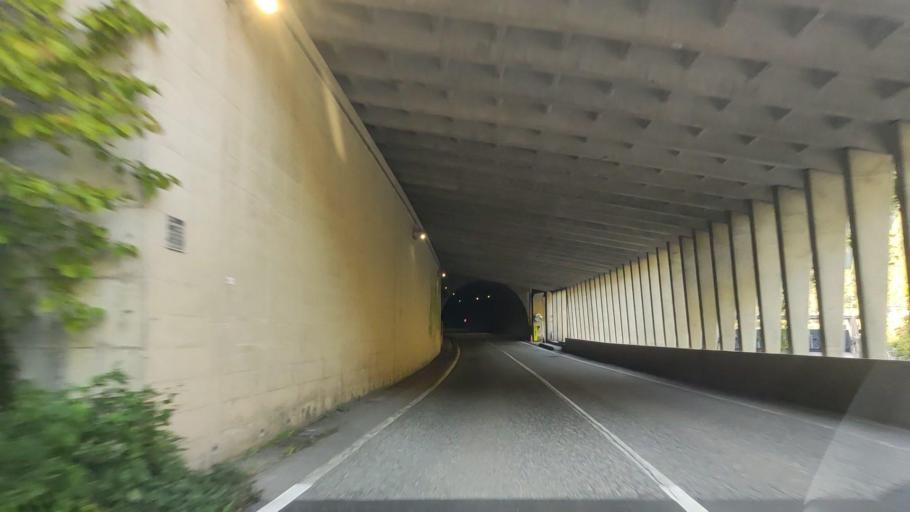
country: JP
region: Gifu
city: Takayama
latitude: 36.3120
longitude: 137.1254
